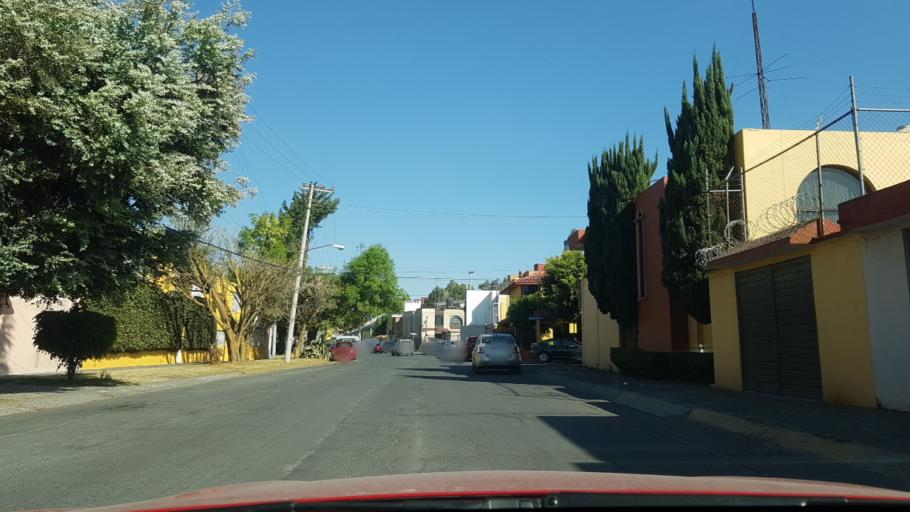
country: MX
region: Mexico
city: Cuautitlan Izcalli
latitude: 19.6463
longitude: -99.2022
